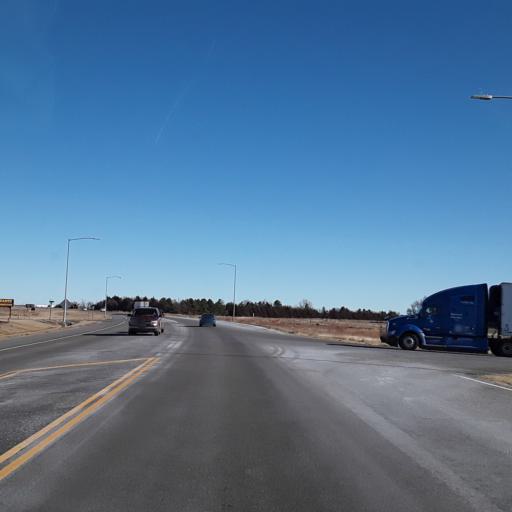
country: US
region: Kansas
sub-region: Pawnee County
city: Larned
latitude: 38.1893
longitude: -99.0842
